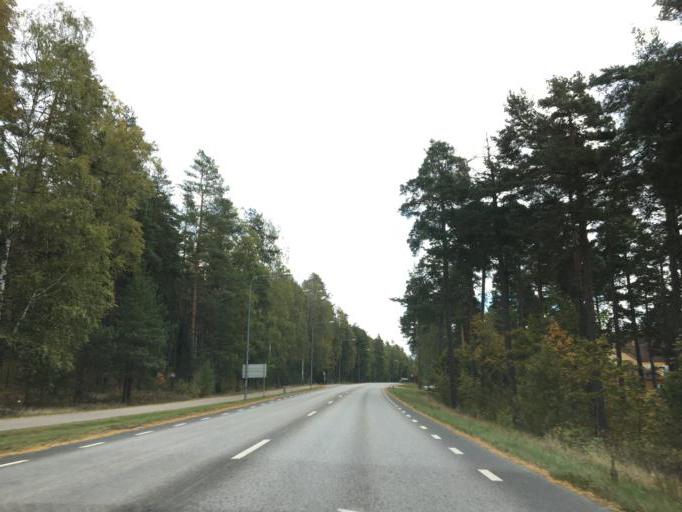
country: SE
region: Soedermanland
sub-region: Katrineholms Kommun
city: Katrineholm
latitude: 58.9859
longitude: 16.2187
